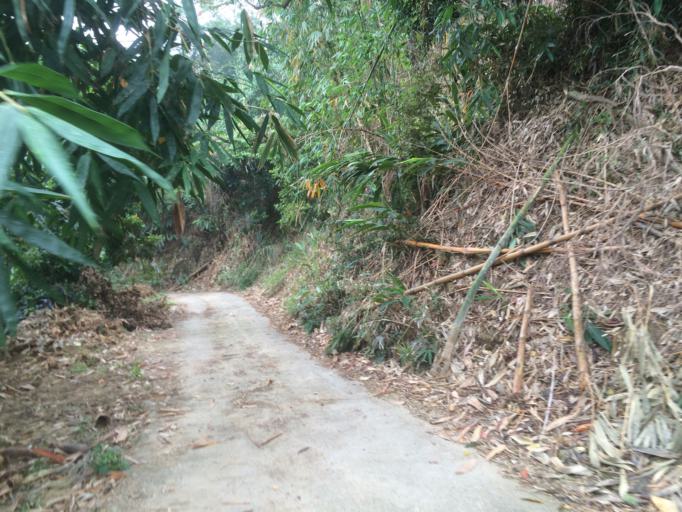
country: TW
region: Taiwan
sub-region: Taichung City
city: Taichung
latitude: 24.1657
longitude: 120.7823
